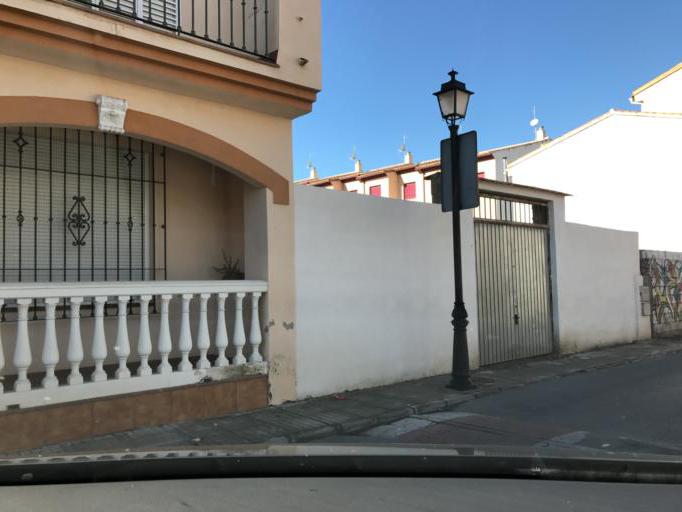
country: ES
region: Andalusia
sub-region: Provincia de Granada
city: Churriana de la Vega
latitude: 37.1386
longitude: -3.6619
